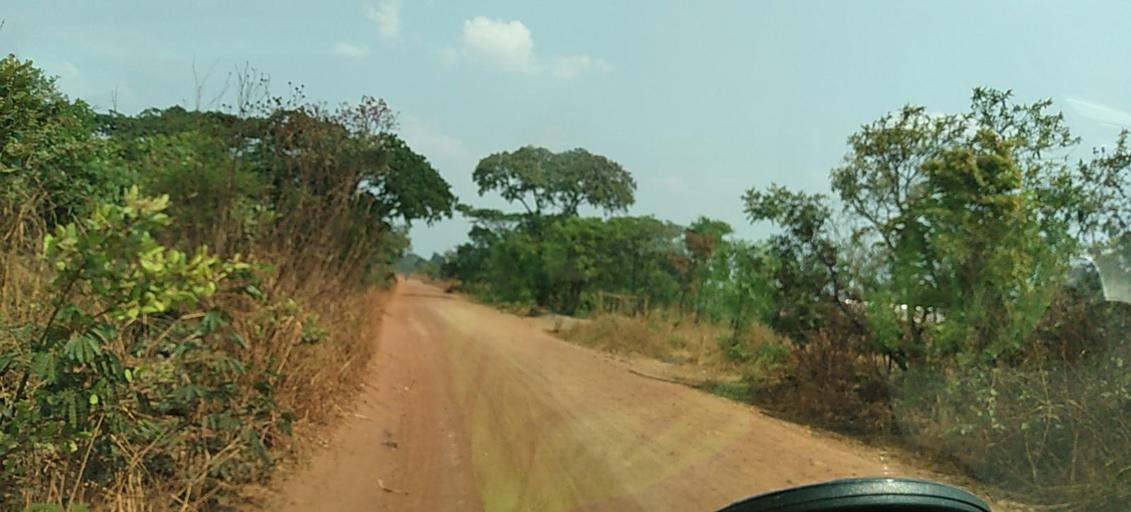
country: ZM
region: North-Western
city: Kansanshi
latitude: -12.0995
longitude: 26.3635
